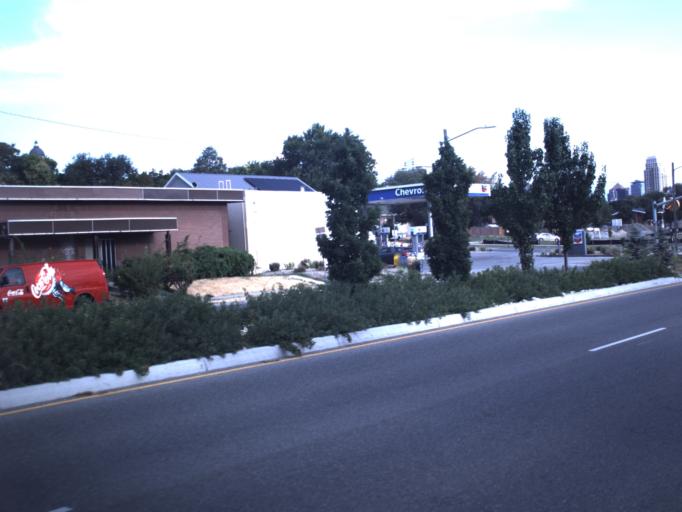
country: US
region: Utah
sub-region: Salt Lake County
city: Salt Lake City
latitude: 40.7834
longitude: -111.8998
